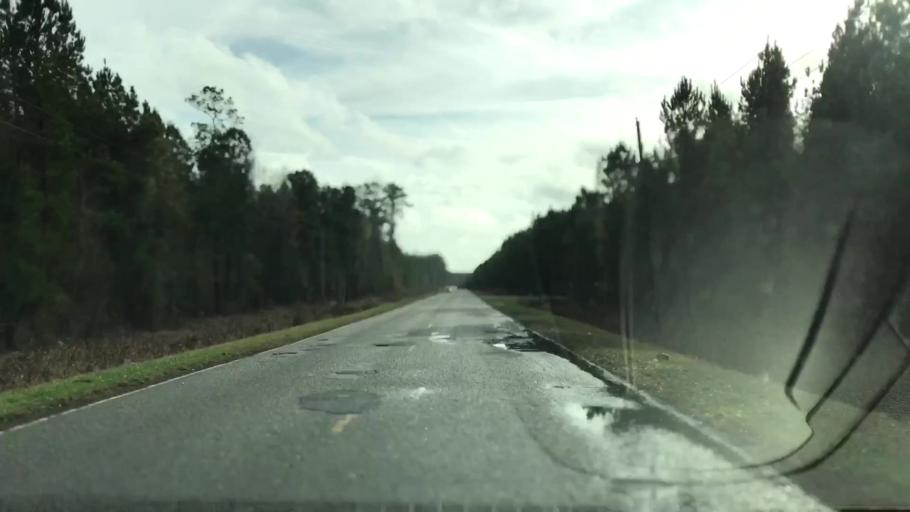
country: US
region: South Carolina
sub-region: Williamsburg County
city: Andrews
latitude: 33.4299
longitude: -79.5940
